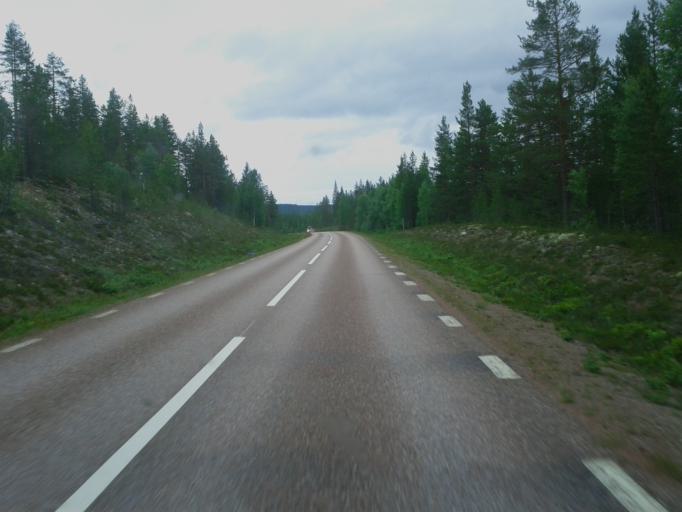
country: NO
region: Hedmark
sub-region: Trysil
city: Innbygda
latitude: 61.7025
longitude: 13.0263
